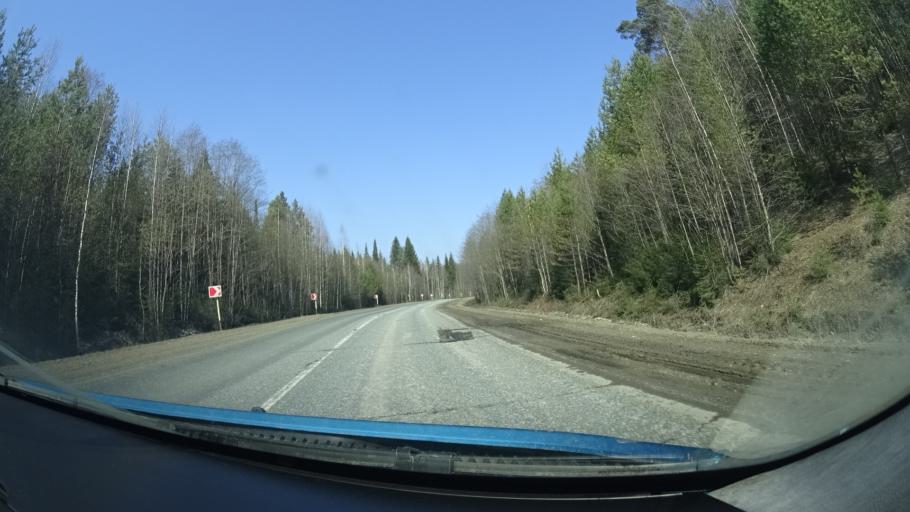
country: RU
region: Perm
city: Yugo-Kamskiy
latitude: 57.5263
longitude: 55.6839
